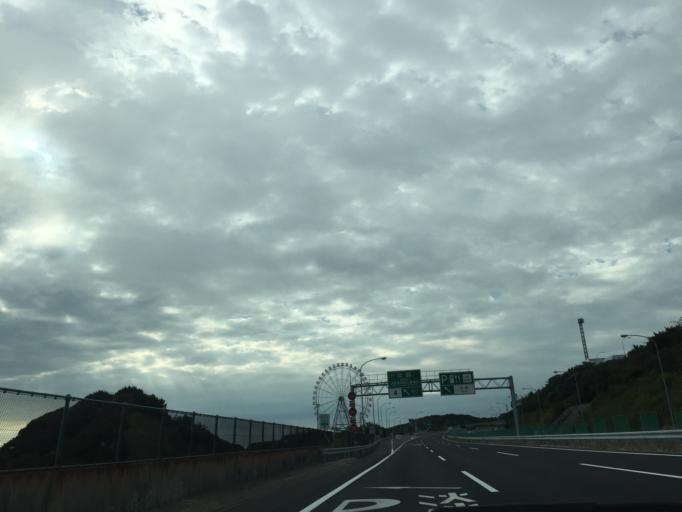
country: JP
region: Hyogo
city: Akashi
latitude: 34.5878
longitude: 135.0130
